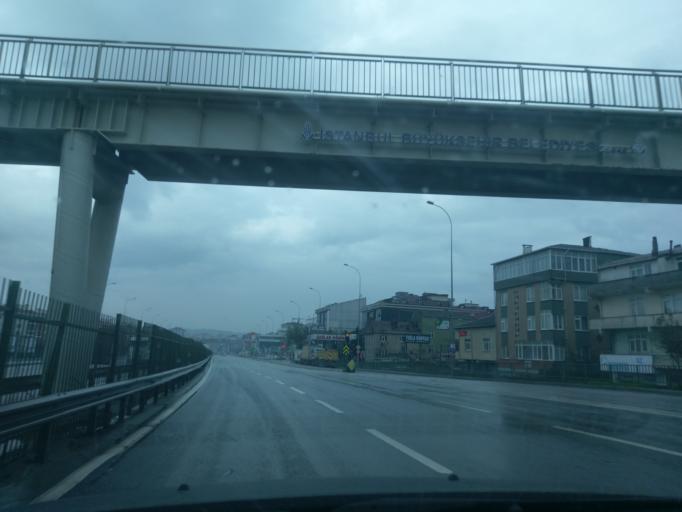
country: TR
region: Istanbul
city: Sancaktepe
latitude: 41.0235
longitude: 29.2219
